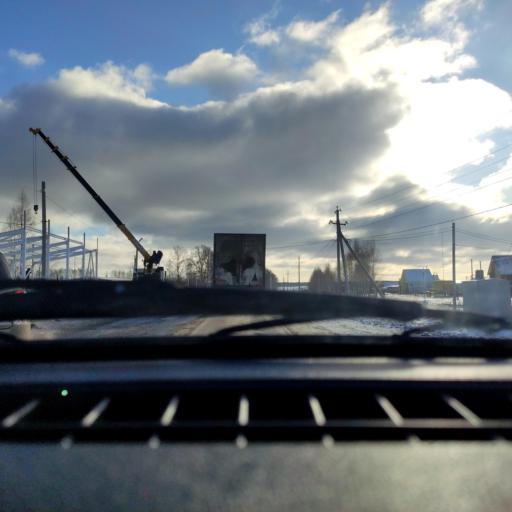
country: RU
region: Bashkortostan
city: Iglino
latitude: 54.8125
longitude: 56.4084
